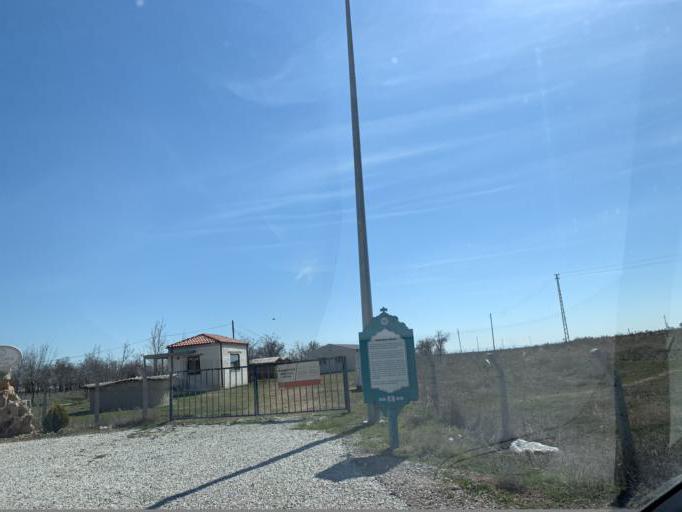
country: TR
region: Konya
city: Yarma
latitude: 37.7522
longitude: 32.8652
